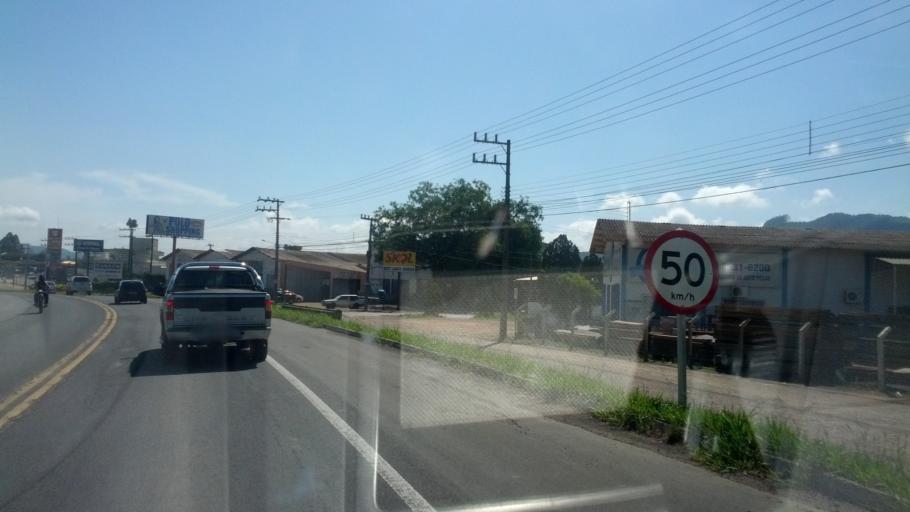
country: BR
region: Santa Catarina
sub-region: Rio Do Sul
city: Rio do Sul
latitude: -27.2044
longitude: -49.6367
